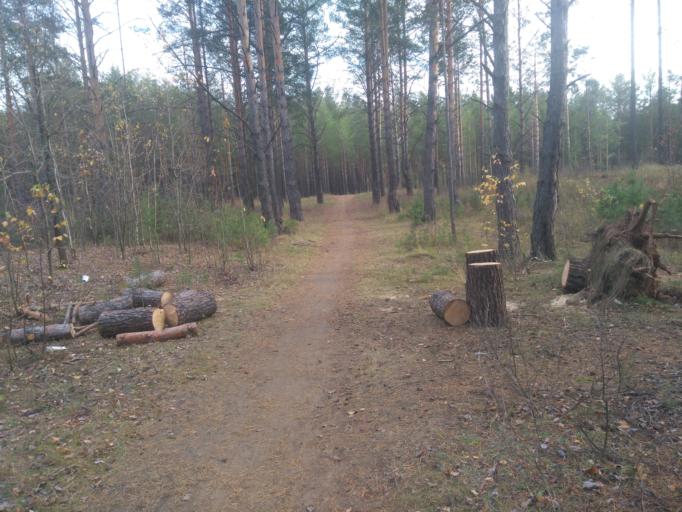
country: RU
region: Tatarstan
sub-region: Tukayevskiy Rayon
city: Naberezhnyye Chelny
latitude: 55.7554
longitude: 52.3810
